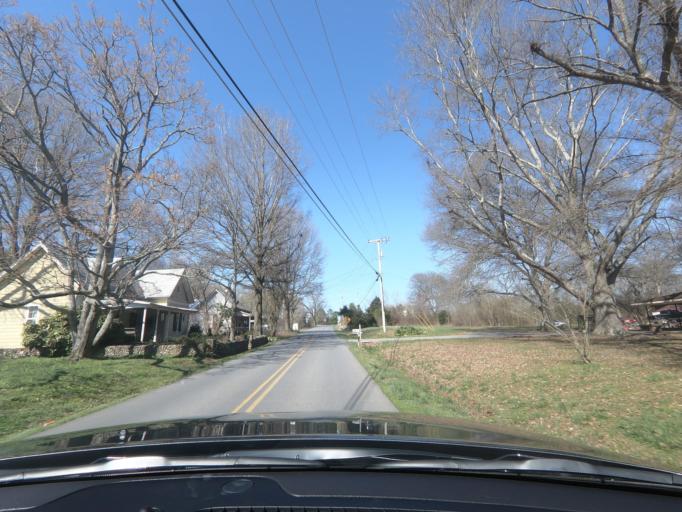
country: US
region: Georgia
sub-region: Bartow County
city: Rydal
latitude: 34.4465
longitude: -84.8093
